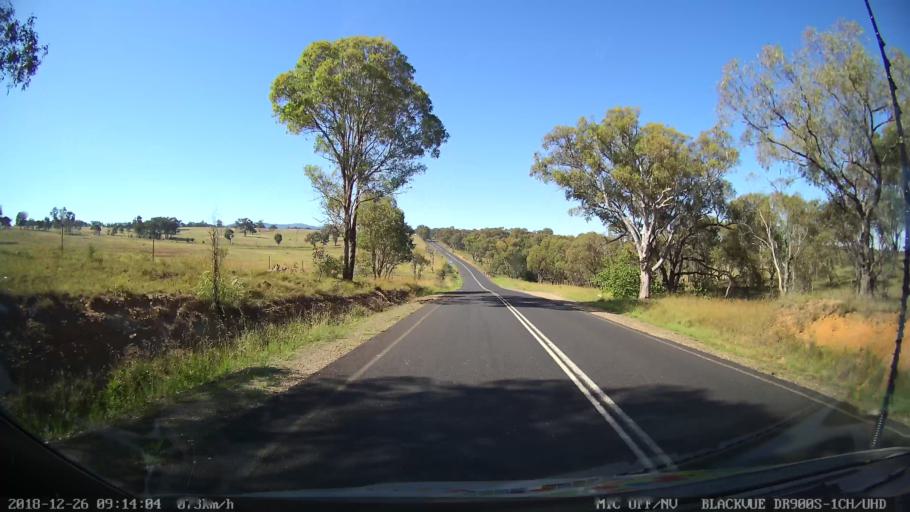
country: AU
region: New South Wales
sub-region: Mid-Western Regional
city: Kandos
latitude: -32.7745
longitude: 149.9796
